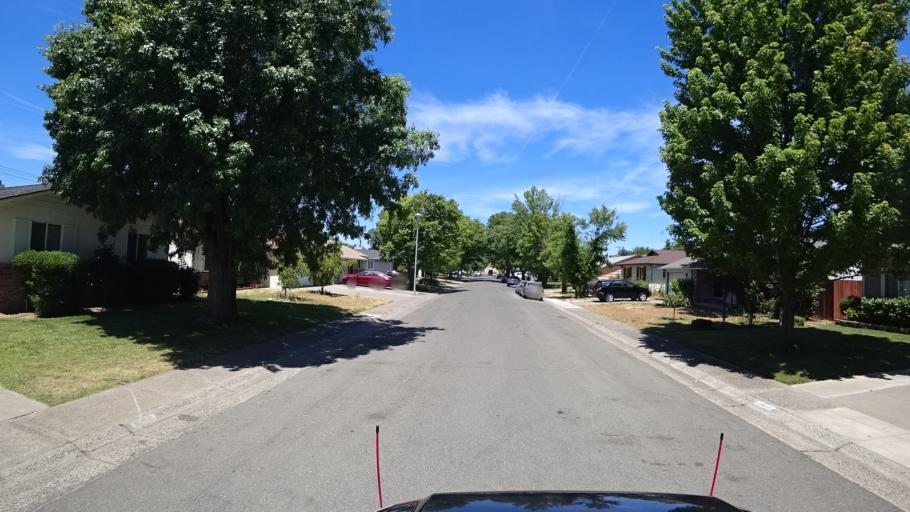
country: US
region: California
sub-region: Sacramento County
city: Parkway
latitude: 38.5219
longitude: -121.4840
